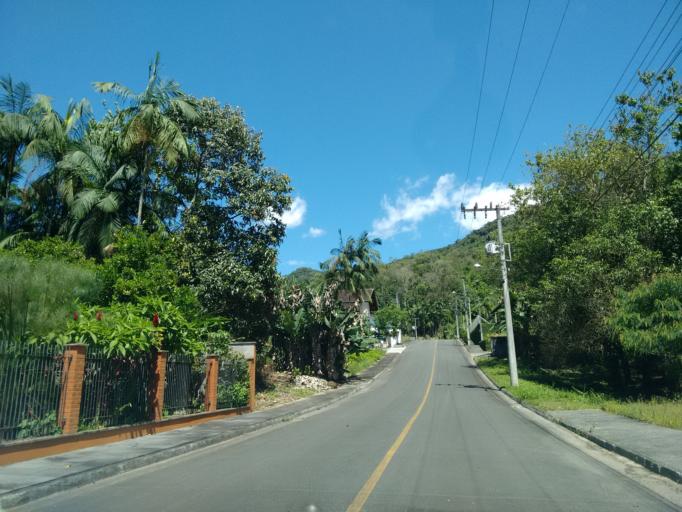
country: BR
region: Santa Catarina
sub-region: Pomerode
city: Pomerode
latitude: -26.7449
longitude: -49.1776
